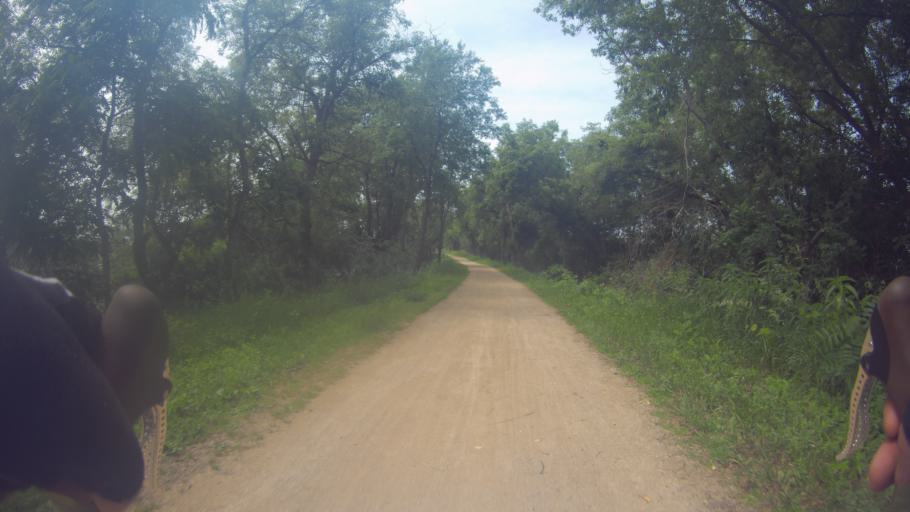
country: US
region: Wisconsin
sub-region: Dane County
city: Mount Horeb
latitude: 43.0123
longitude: -89.7242
